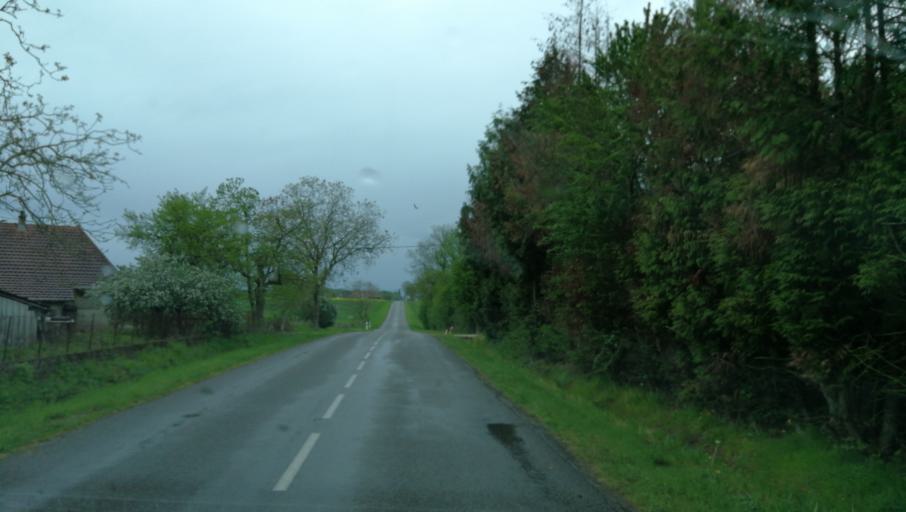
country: FR
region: Franche-Comte
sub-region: Departement du Jura
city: Bletterans
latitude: 46.8141
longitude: 5.3908
